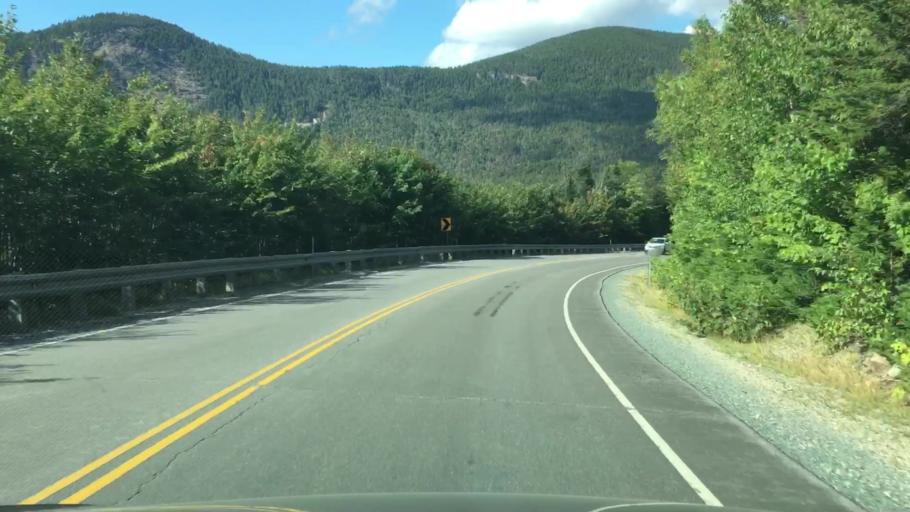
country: US
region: New Hampshire
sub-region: Grafton County
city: Woodstock
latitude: 44.0316
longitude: -71.4992
